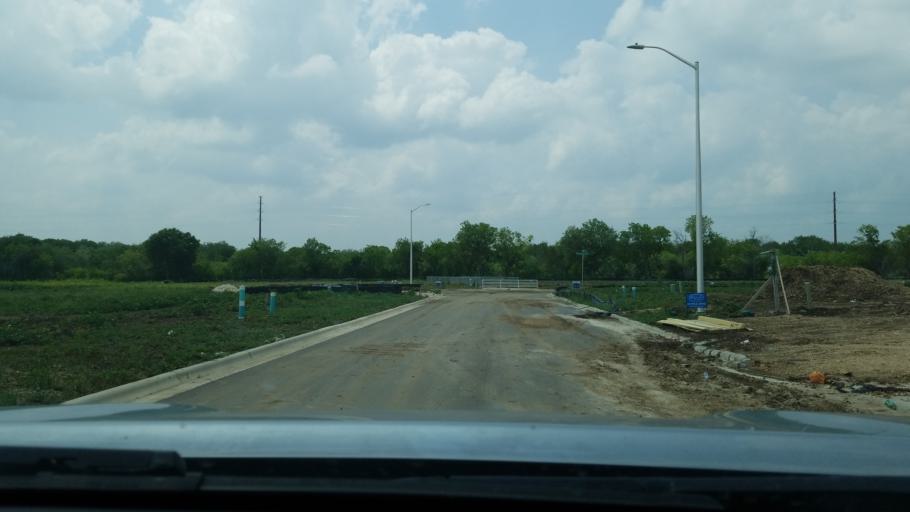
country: US
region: Texas
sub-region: Comal County
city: New Braunfels
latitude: 29.7474
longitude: -98.0967
